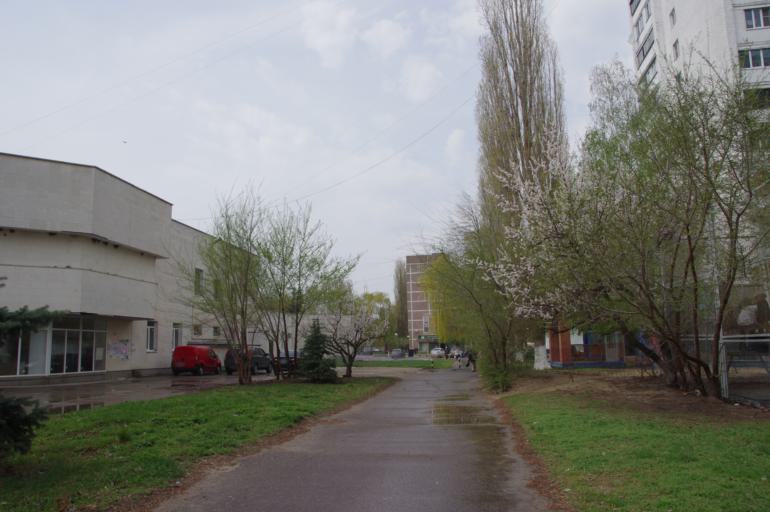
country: RU
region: Kursk
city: Kurchatov
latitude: 51.6607
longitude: 35.6585
